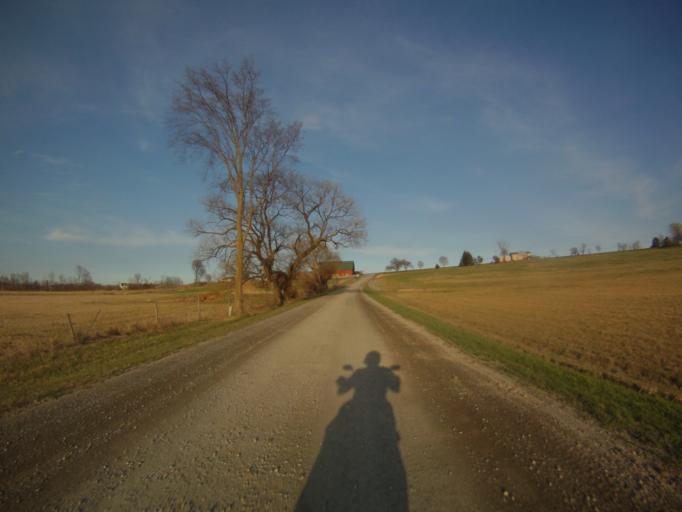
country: US
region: Vermont
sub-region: Addison County
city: Vergennes
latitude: 44.0964
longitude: -73.3036
